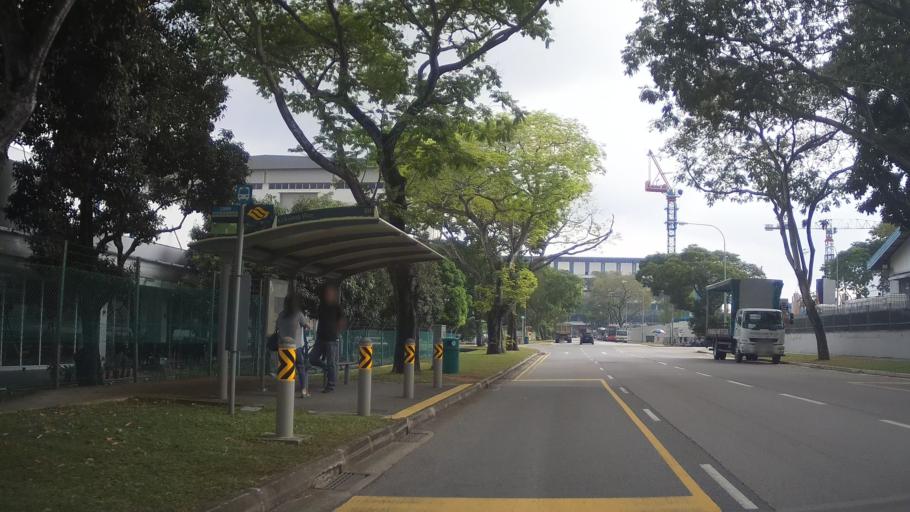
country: MY
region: Johor
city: Johor Bahru
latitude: 1.3246
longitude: 103.6926
